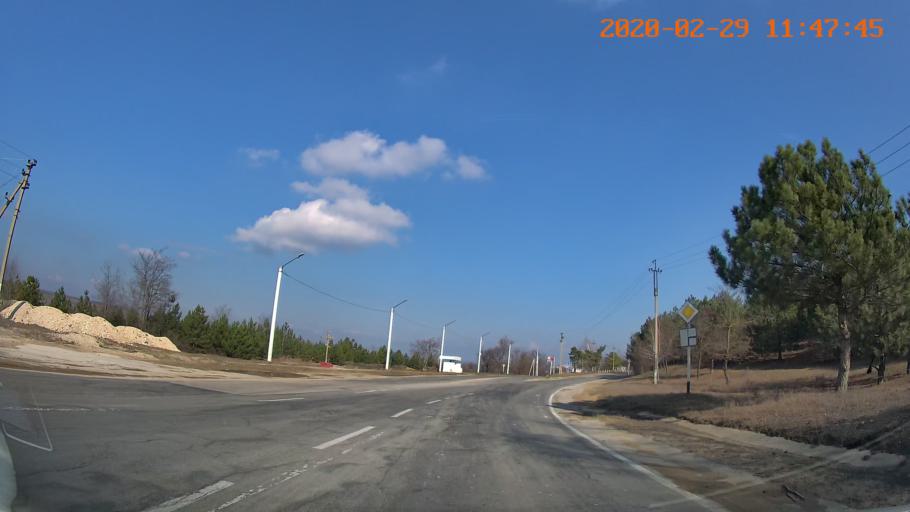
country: MD
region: Rezina
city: Rezina
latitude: 47.7432
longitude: 28.9872
